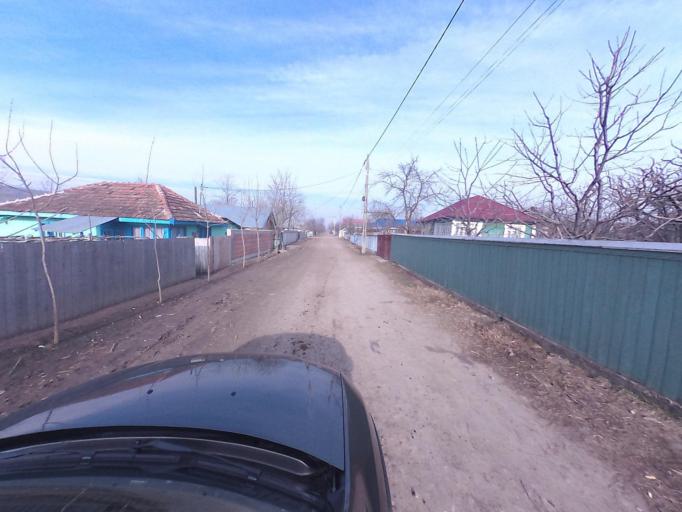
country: RO
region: Vaslui
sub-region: Comuna Solesti
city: Solesti
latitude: 46.8066
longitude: 27.7846
